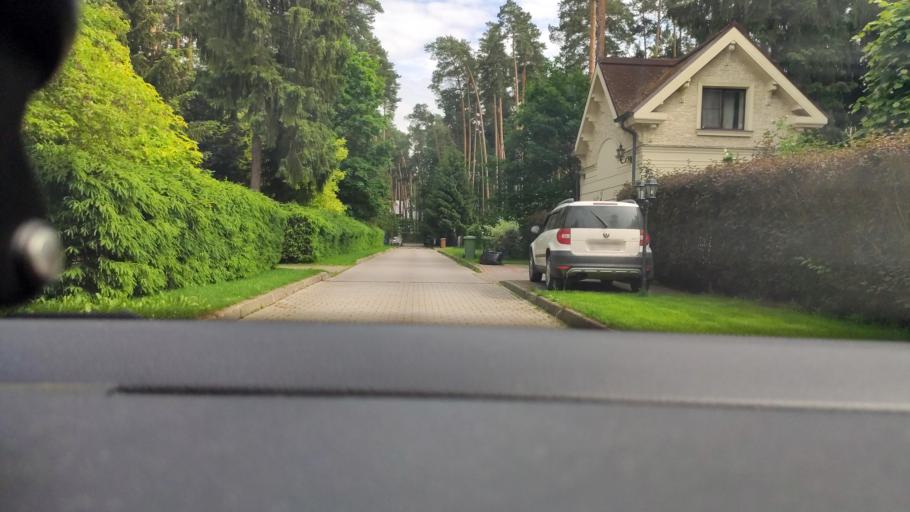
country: RU
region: Moskovskaya
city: Nikolina Gora
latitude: 55.7343
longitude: 37.0724
